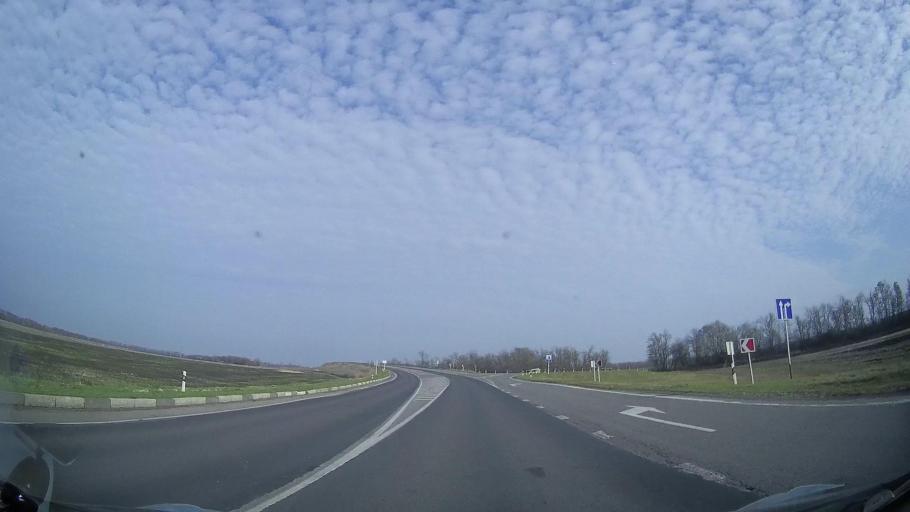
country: RU
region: Rostov
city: Tselina
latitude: 46.5248
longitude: 41.1649
